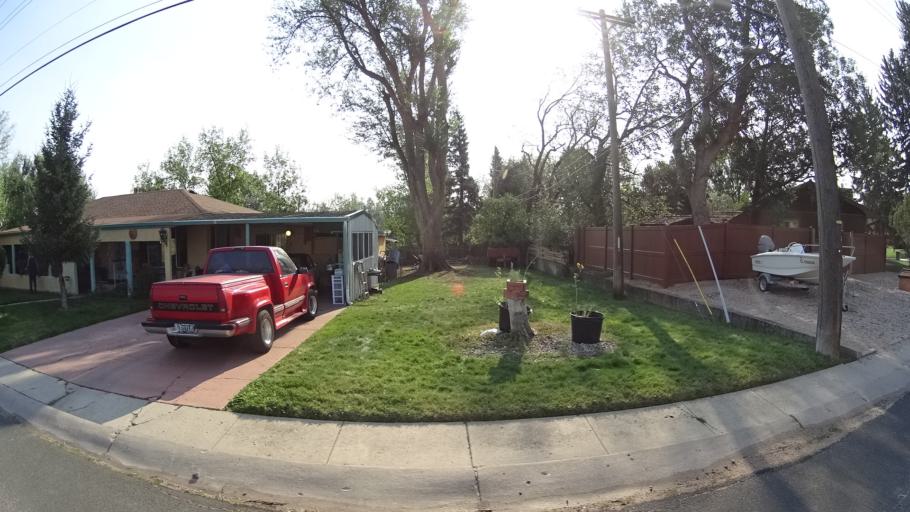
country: US
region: Colorado
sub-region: El Paso County
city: Colorado Springs
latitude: 38.8044
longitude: -104.8502
